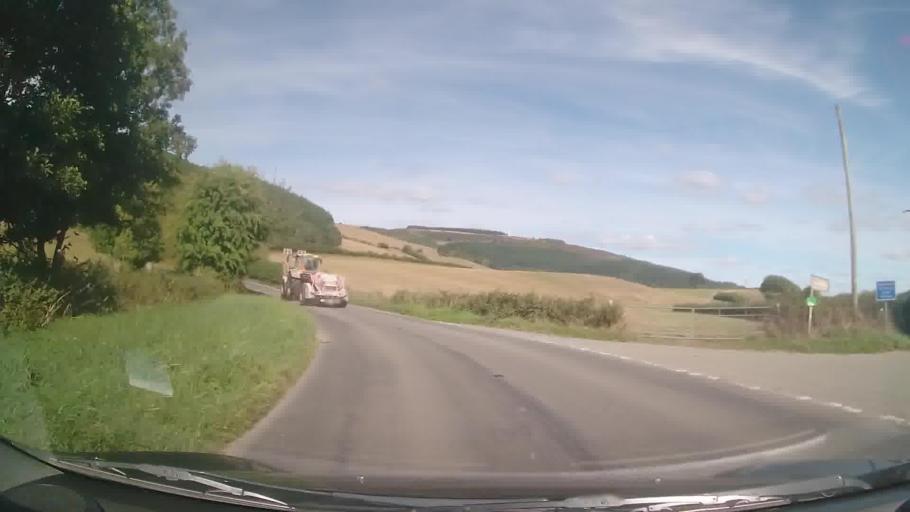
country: GB
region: Wales
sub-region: Sir Powys
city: Knighton
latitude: 52.3487
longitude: -3.0271
